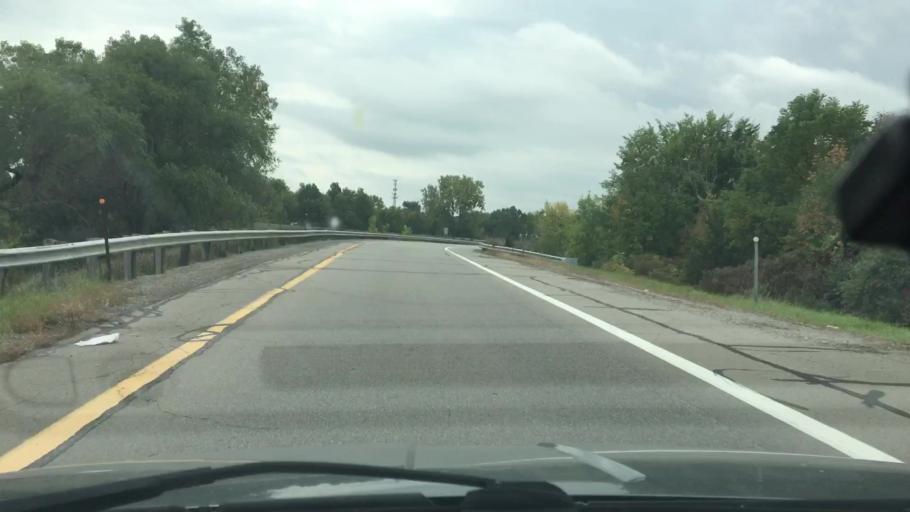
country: US
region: Michigan
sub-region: Genesee County
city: Fenton
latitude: 42.8027
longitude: -83.7311
